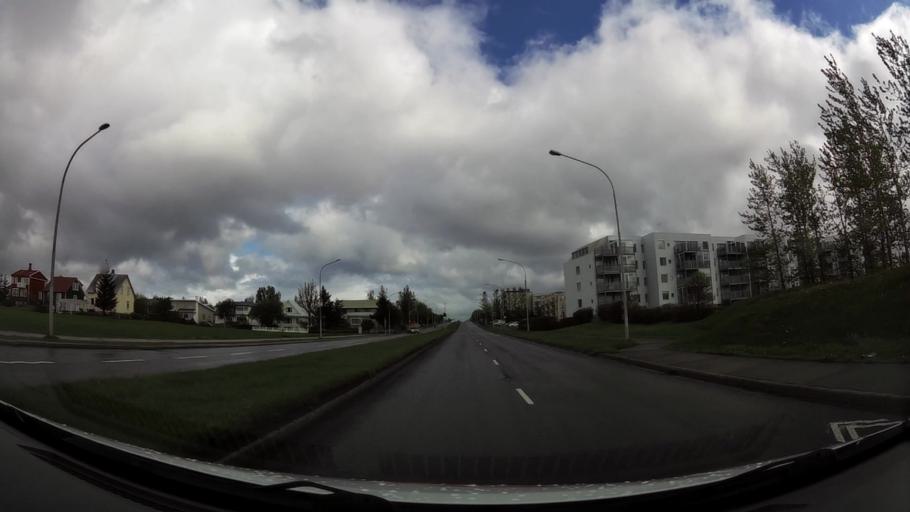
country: IS
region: Capital Region
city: Seltjarnarnes
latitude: 64.1343
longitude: -21.9578
